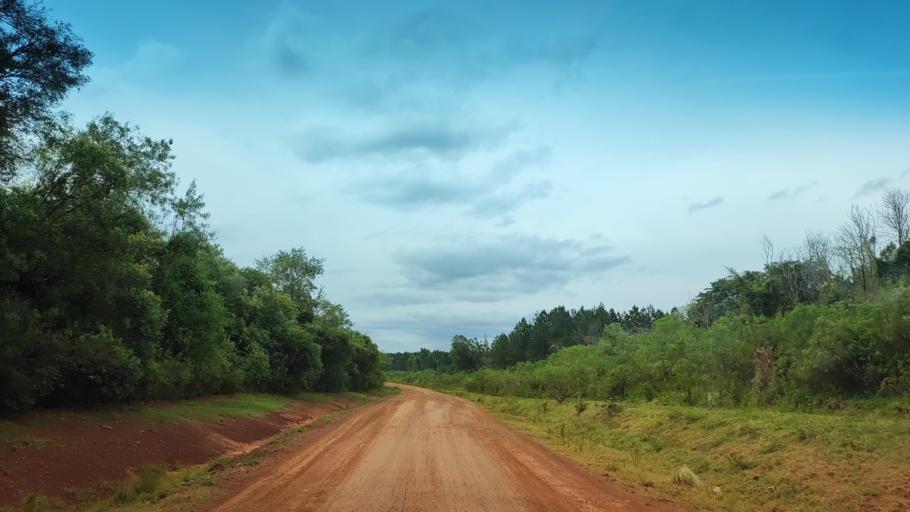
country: AR
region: Misiones
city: Garupa
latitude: -27.5069
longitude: -55.9701
